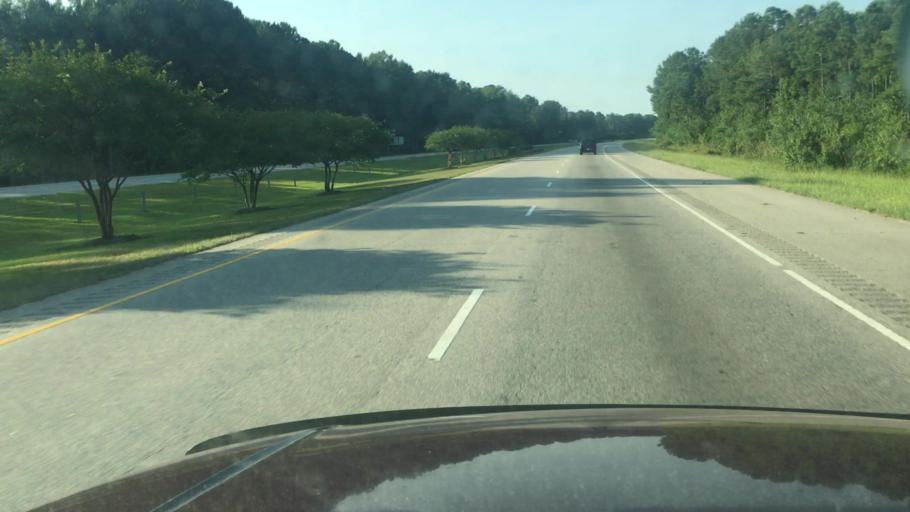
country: US
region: North Carolina
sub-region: Cumberland County
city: Fayetteville
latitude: 34.9985
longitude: -78.8642
